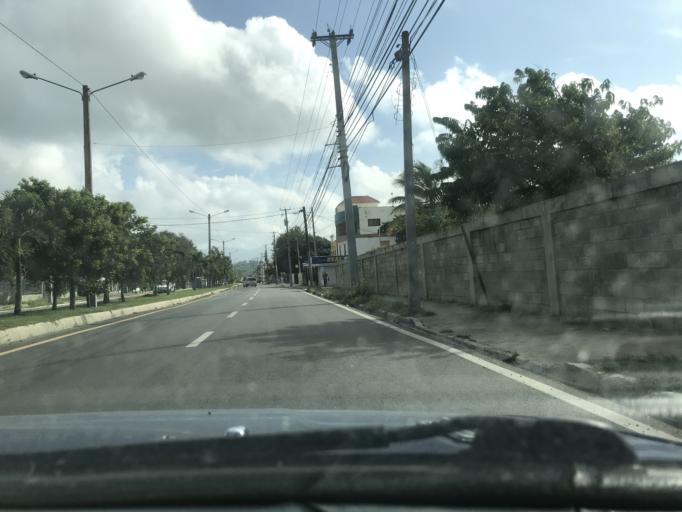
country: DO
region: Santiago
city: Santiago de los Caballeros
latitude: 19.4319
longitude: -70.7254
